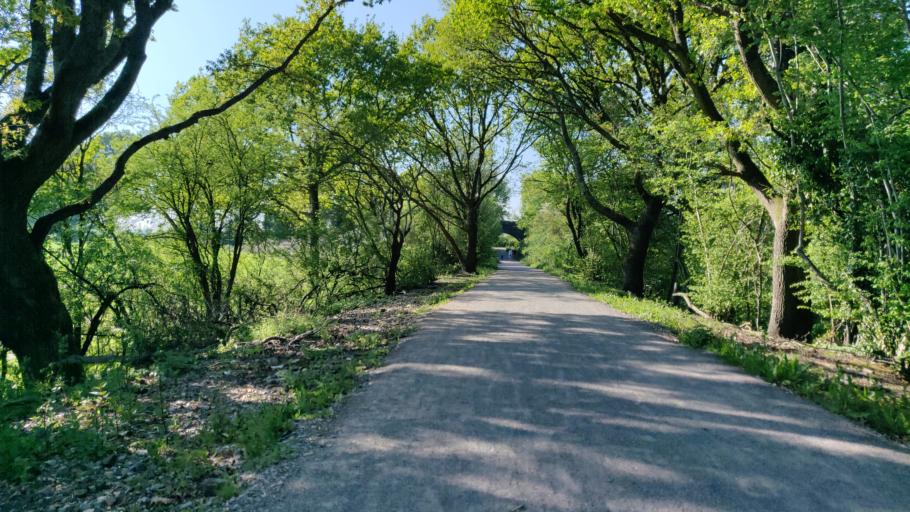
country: GB
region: England
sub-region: West Sussex
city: Southwater
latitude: 51.0541
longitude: -0.3743
